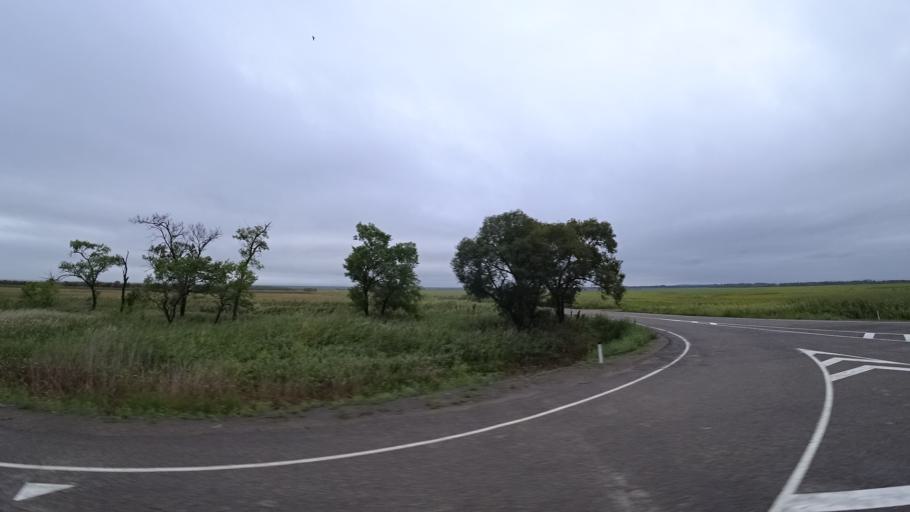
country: RU
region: Primorskiy
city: Chernigovka
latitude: 44.2982
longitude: 132.5232
